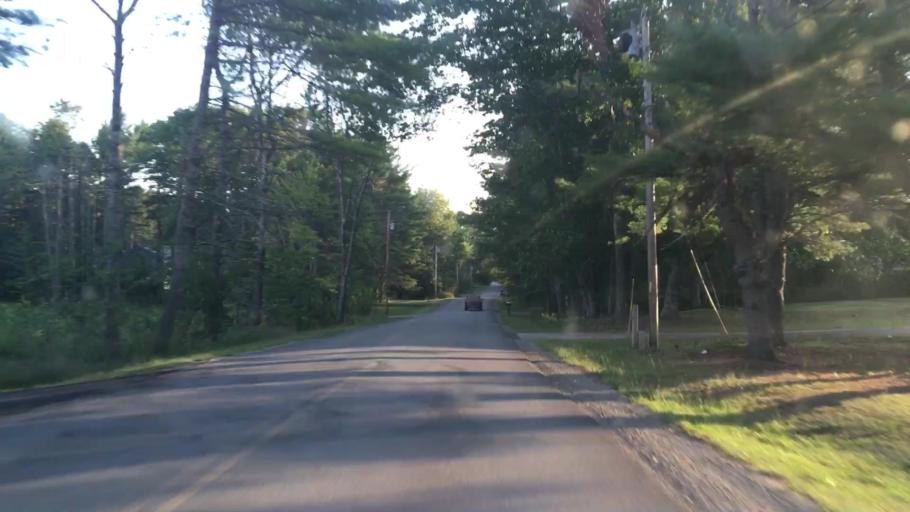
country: US
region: Maine
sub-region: Waldo County
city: Winterport
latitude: 44.6953
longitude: -68.8990
